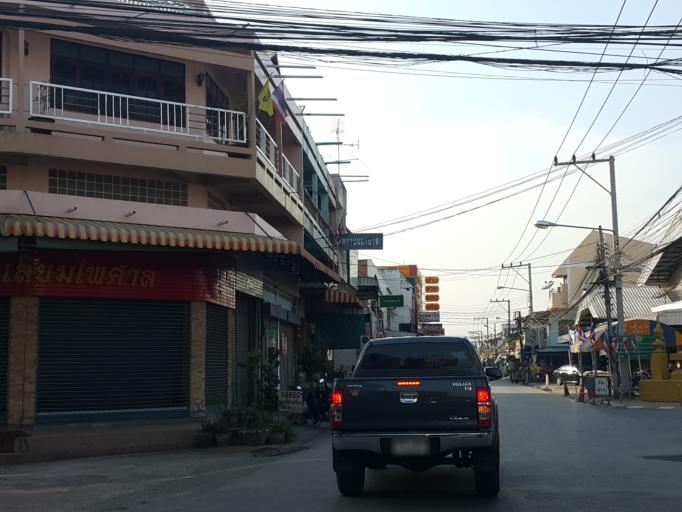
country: TH
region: Phitsanulok
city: Phrom Phiram
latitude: 17.1017
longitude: 100.1662
